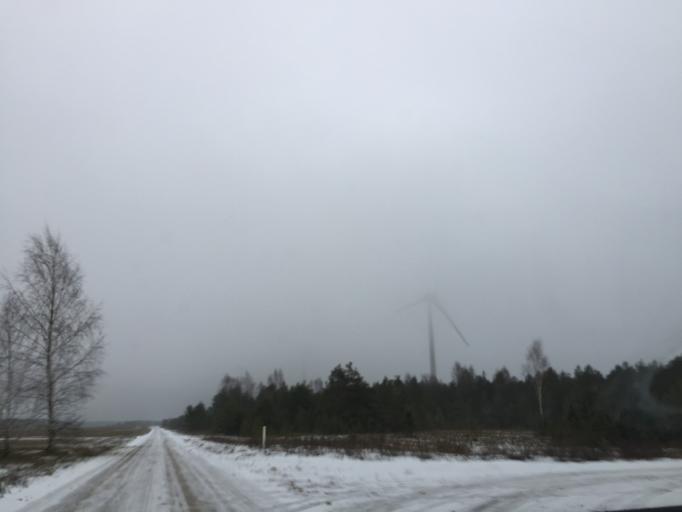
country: EE
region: Laeaene
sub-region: Lihula vald
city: Lihula
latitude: 58.6274
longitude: 23.5346
